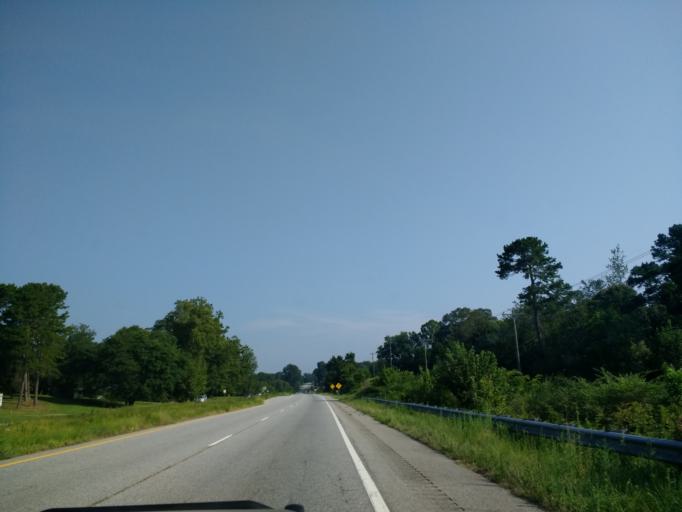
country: US
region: Georgia
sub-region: Hall County
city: Gainesville
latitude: 34.4087
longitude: -83.8053
